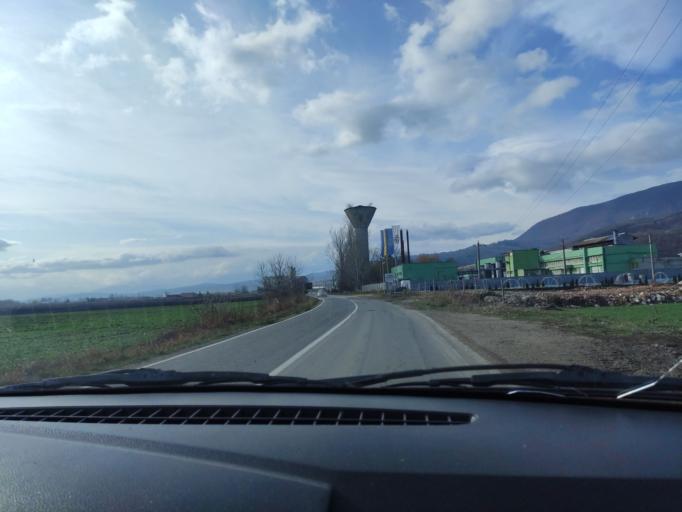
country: RO
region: Brasov
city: Codlea
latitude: 45.7156
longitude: 25.4699
